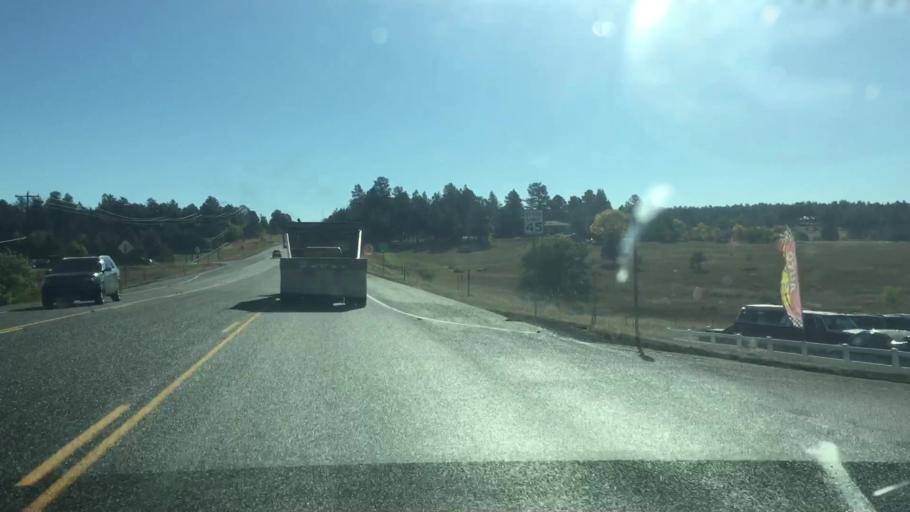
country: US
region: Colorado
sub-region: Douglas County
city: The Pinery
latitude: 39.3903
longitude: -104.7490
